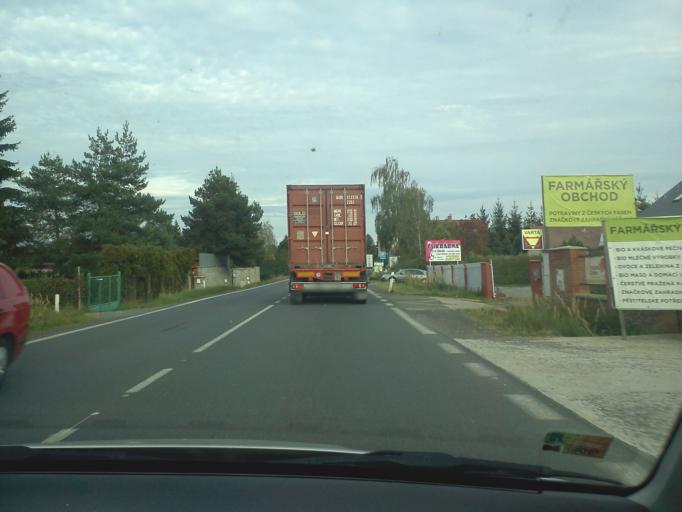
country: CZ
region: Central Bohemia
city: Mukarov
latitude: 49.9899
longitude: 14.7309
